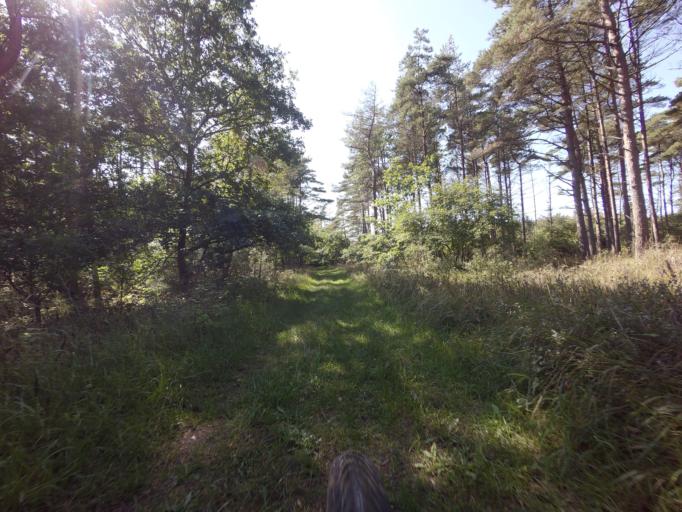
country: DK
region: North Denmark
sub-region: Hjorring Kommune
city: Hirtshals
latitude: 57.5865
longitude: 10.0042
